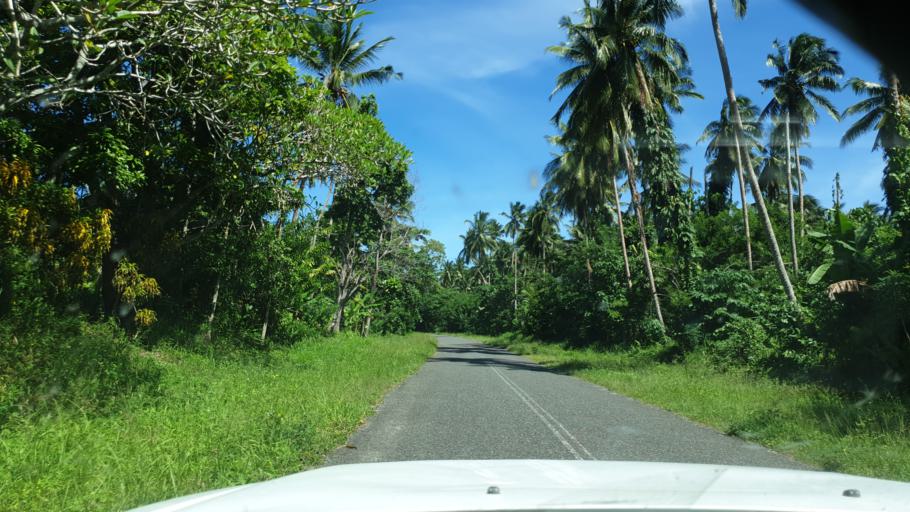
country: PG
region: Madang
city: Madang
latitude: -4.4791
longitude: 145.4211
